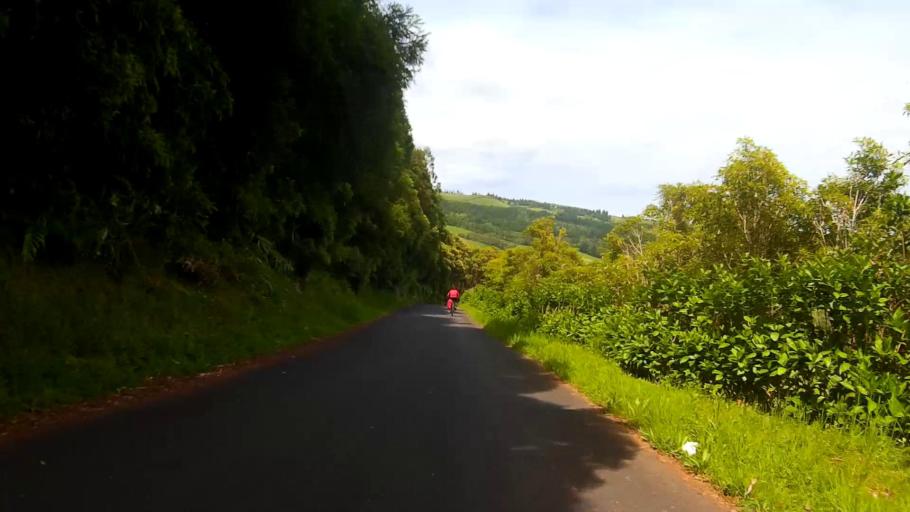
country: PT
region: Azores
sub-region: Horta
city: Horta
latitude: 38.5516
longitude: -28.6698
